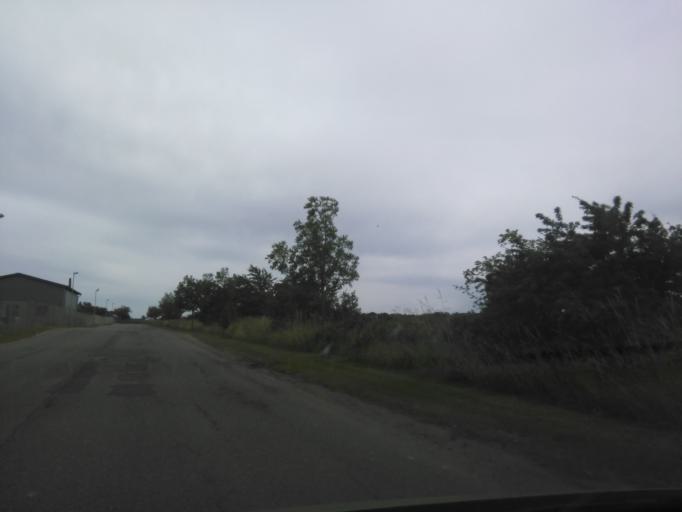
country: DK
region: Central Jutland
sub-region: Horsens Kommune
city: Horsens
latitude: 55.8549
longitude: 9.8614
